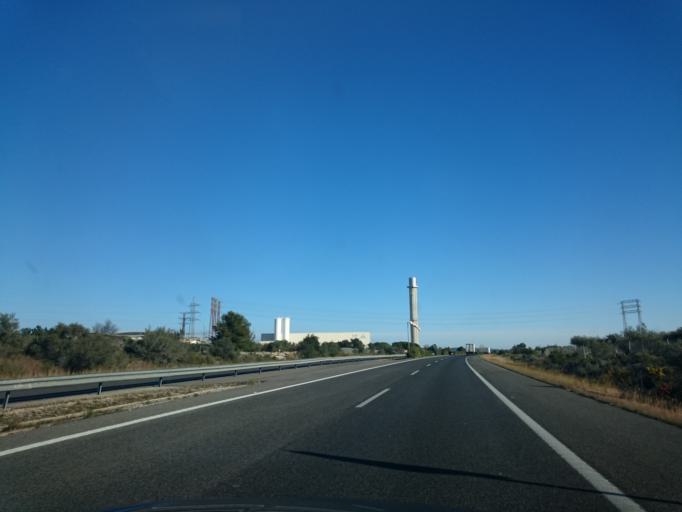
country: ES
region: Catalonia
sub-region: Provincia de Tarragona
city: Camarles
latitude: 40.7980
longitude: 0.6703
